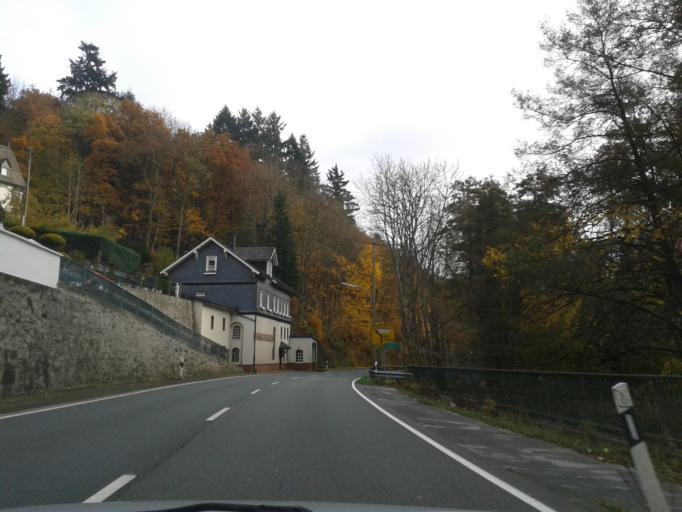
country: DE
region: North Rhine-Westphalia
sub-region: Regierungsbezirk Arnsberg
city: Bad Laasphe
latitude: 50.9238
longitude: 8.3993
